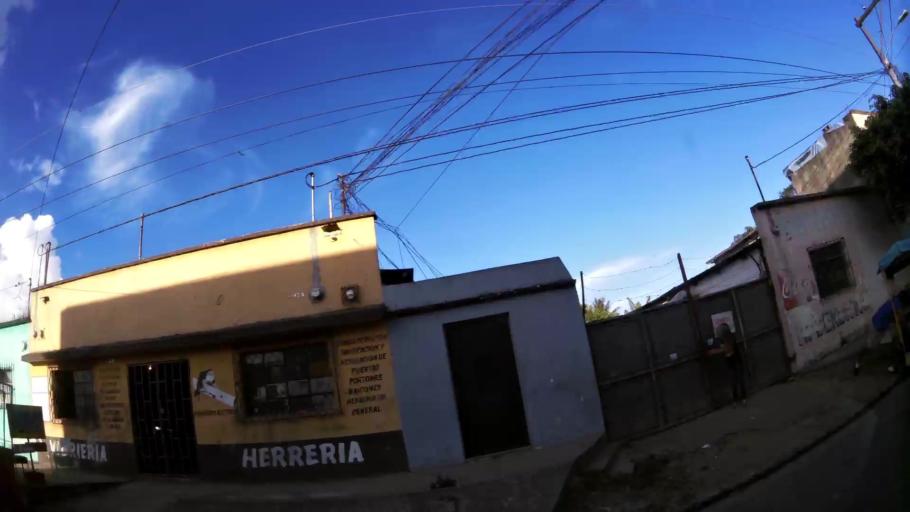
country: GT
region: Guatemala
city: Villa Nueva
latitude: 14.5212
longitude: -90.5871
